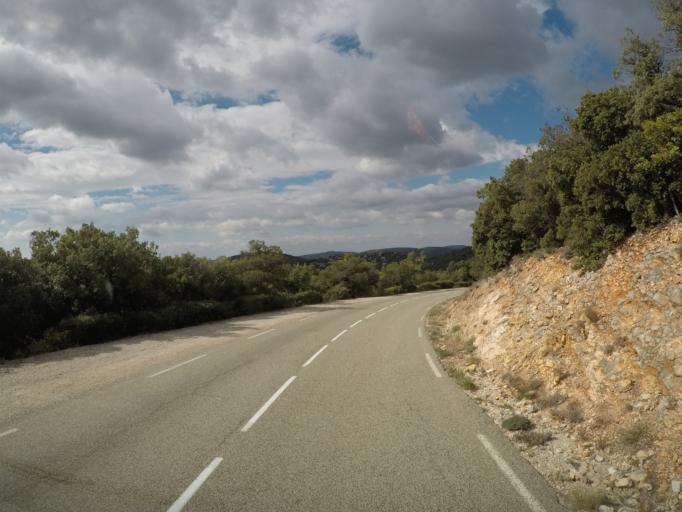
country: FR
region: Rhone-Alpes
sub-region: Departement de la Drome
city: Buis-les-Baronnies
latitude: 44.2227
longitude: 5.2042
